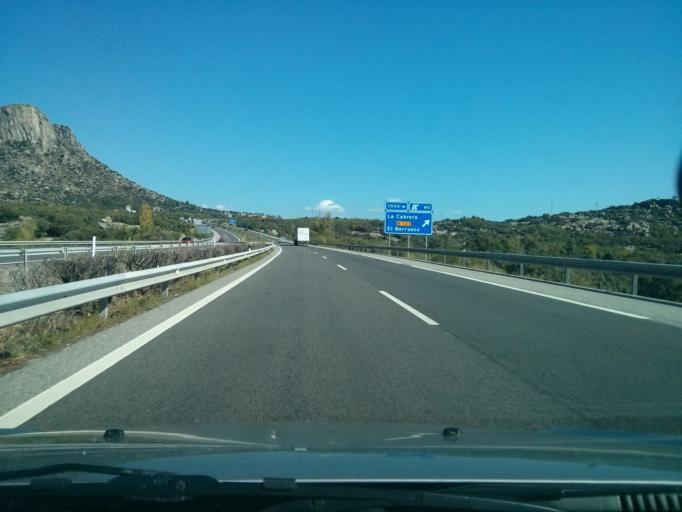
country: ES
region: Madrid
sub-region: Provincia de Madrid
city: La Cabrera
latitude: 40.8603
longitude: -3.6076
